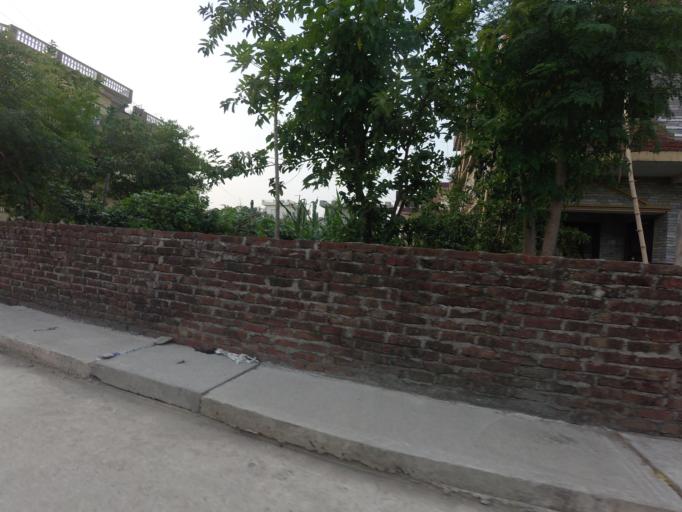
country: NP
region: Western Region
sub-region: Lumbini Zone
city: Bhairahawa
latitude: 27.5143
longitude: 83.4591
